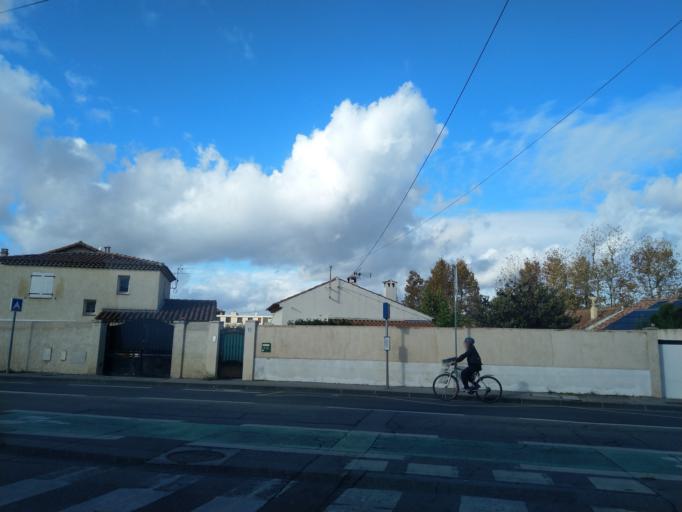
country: FR
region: Provence-Alpes-Cote d'Azur
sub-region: Departement des Bouches-du-Rhone
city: Marseille 12
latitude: 43.3125
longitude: 5.4308
